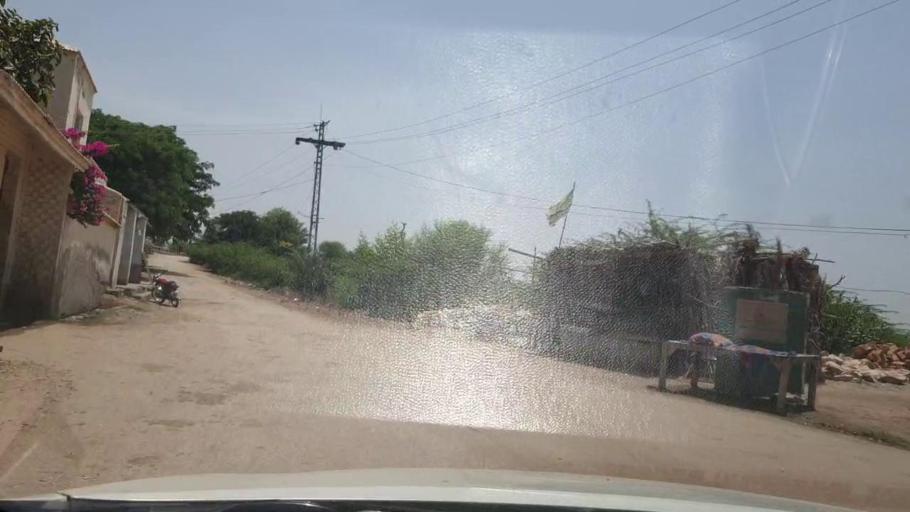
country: PK
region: Sindh
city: Bozdar
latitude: 27.2058
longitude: 68.6665
